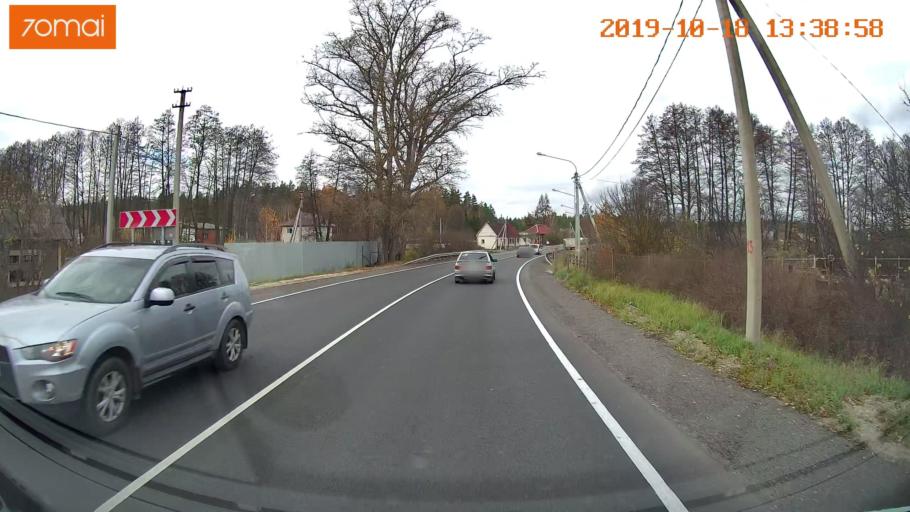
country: RU
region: Rjazan
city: Solotcha
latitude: 54.8942
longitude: 40.0007
